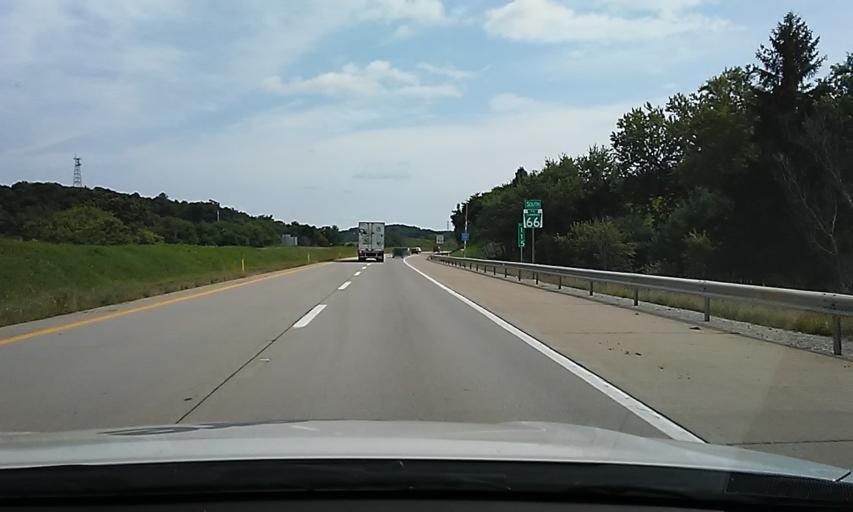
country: US
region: Pennsylvania
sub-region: Westmoreland County
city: Delmont
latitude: 40.3733
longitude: -79.5599
